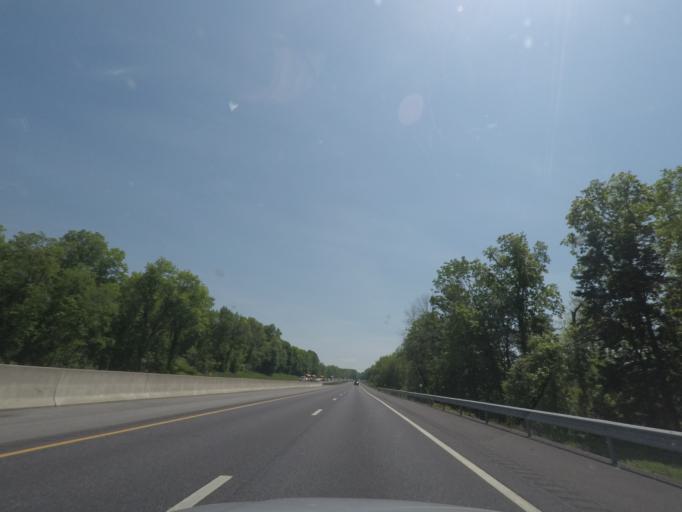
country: US
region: New York
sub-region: Ulster County
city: Clintondale
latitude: 41.6736
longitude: -74.0803
